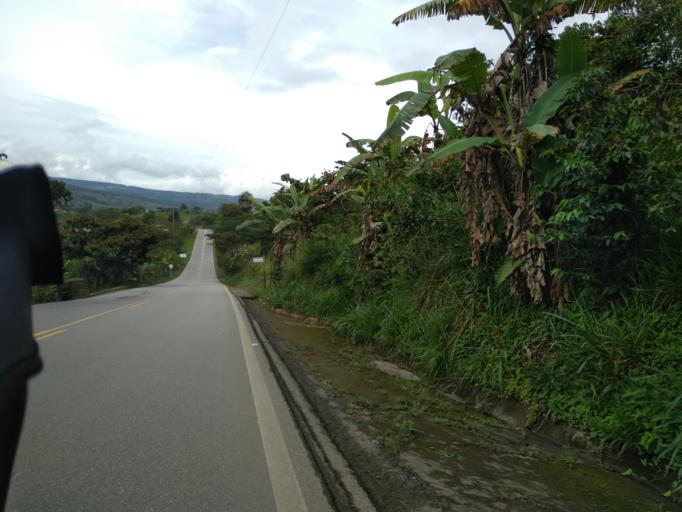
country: CO
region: Santander
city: Suaita
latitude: 6.1299
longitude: -73.3610
